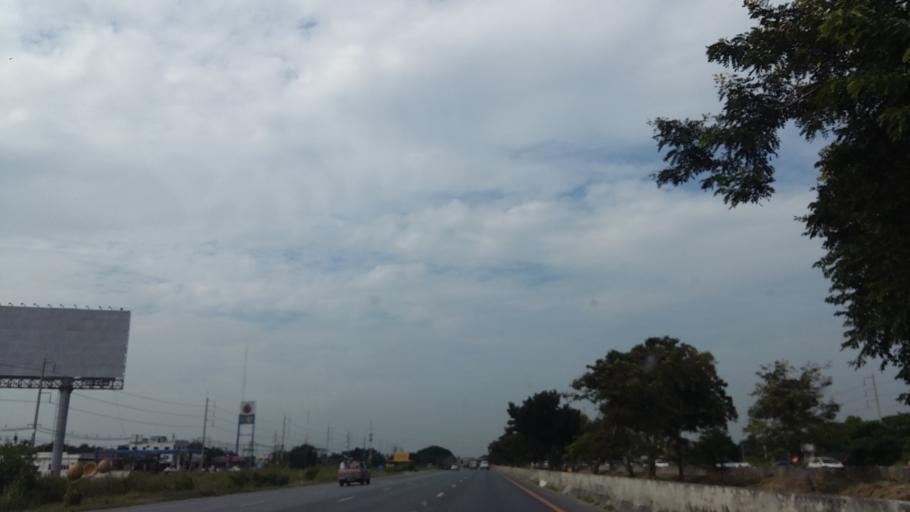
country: TH
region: Phra Nakhon Si Ayutthaya
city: Maha Rat
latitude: 14.5002
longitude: 100.5217
